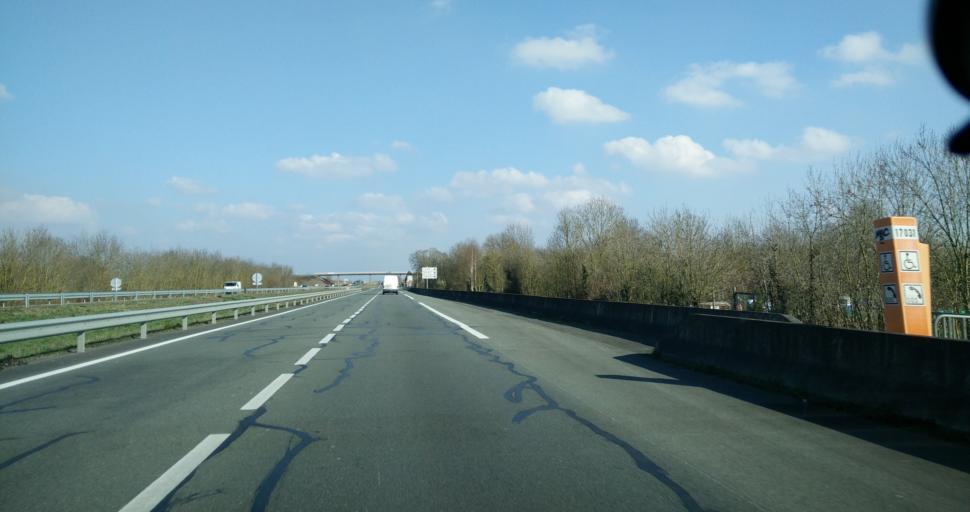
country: FR
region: Poitou-Charentes
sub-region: Departement de la Charente-Maritime
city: Sainte-Soulle
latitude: 46.2125
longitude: -0.9954
